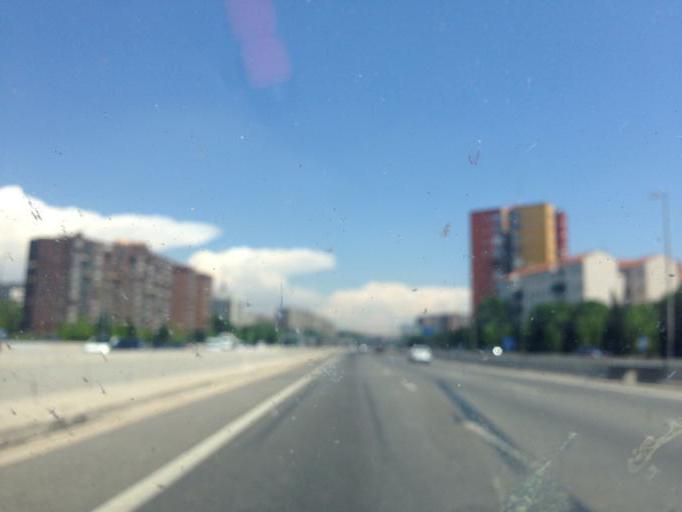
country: ES
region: Madrid
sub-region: Provincia de Madrid
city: Puente de Vallecas
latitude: 40.4016
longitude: -3.6674
